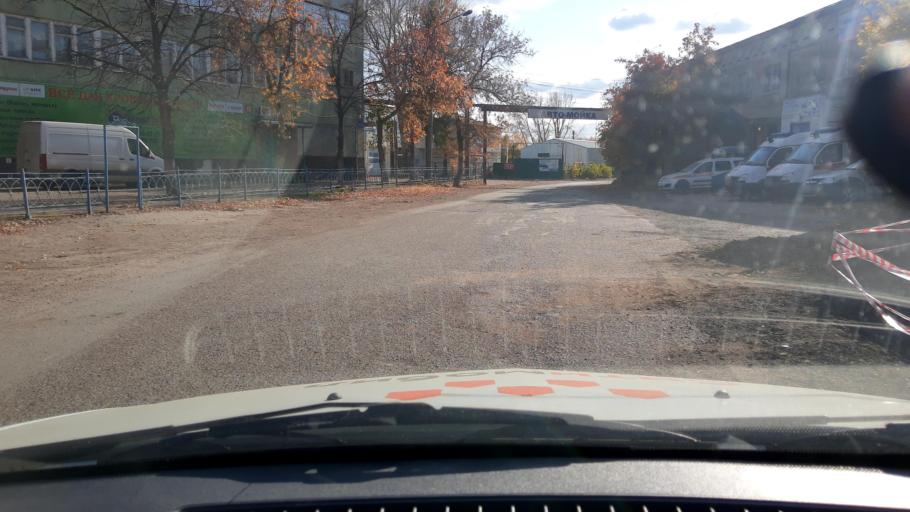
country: RU
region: Bashkortostan
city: Ufa
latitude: 54.7980
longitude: 56.0901
